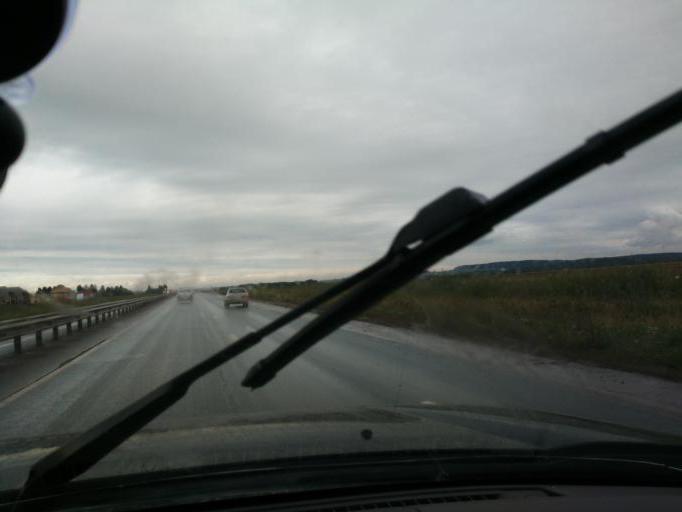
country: RU
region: Perm
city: Kultayevo
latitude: 57.8913
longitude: 55.9503
